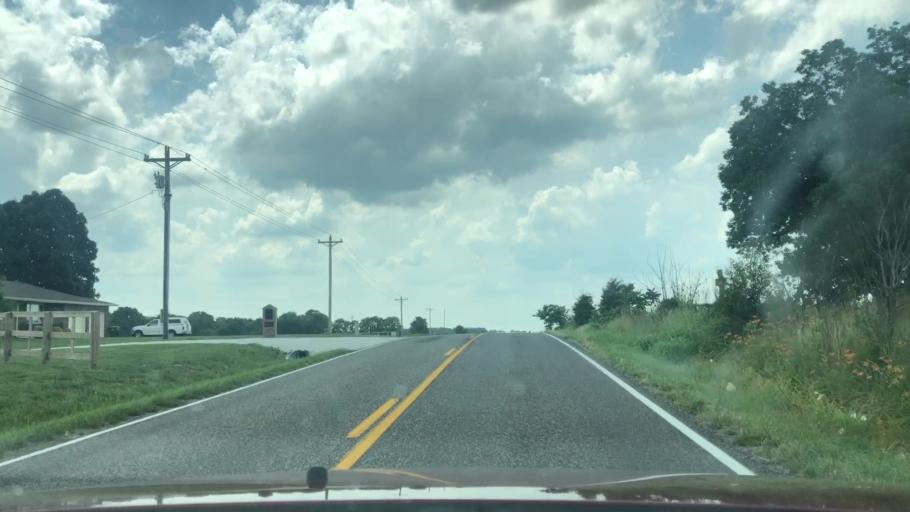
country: US
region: Missouri
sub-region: Christian County
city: Ozark
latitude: 36.9431
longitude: -93.2454
